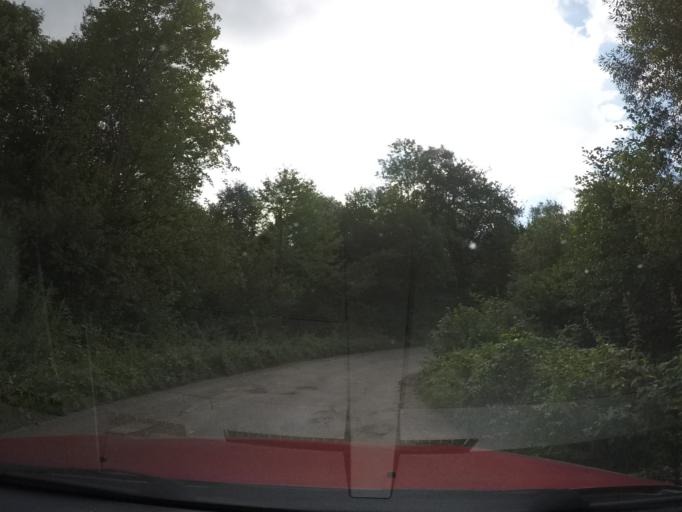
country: UA
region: Zakarpattia
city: Velykyi Bereznyi
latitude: 48.9496
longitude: 22.6739
